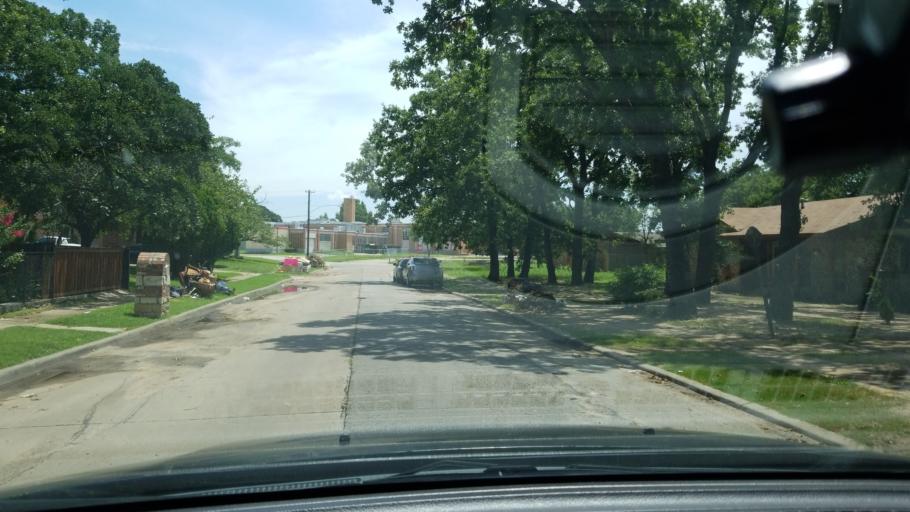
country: US
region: Texas
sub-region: Dallas County
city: Balch Springs
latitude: 32.7408
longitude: -96.6433
